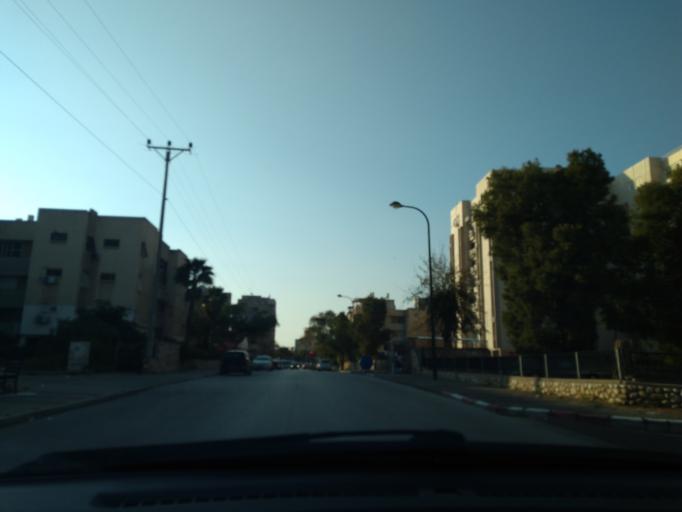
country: IL
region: Central District
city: Even Yehuda
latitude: 32.2820
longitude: 34.8559
